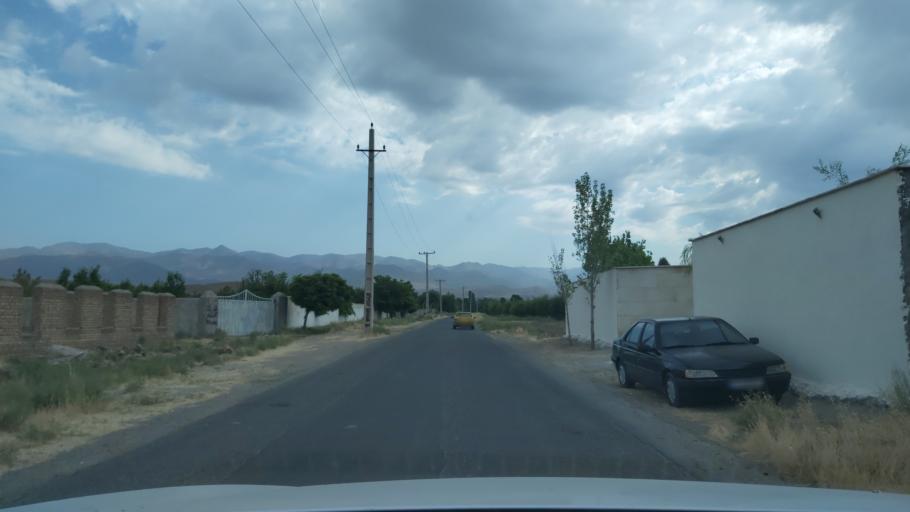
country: IR
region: Alborz
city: Hashtgerd
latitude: 35.9534
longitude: 50.7763
